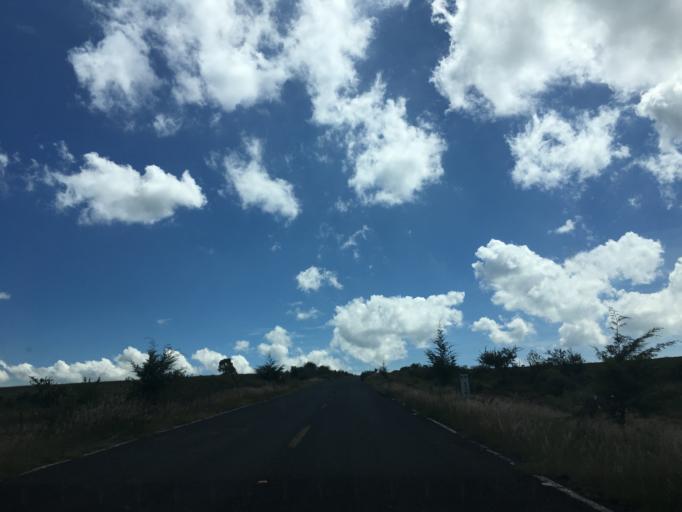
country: MX
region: Michoacan
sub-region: Morelia
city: Cuto de la Esperanza
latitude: 19.7724
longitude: -101.3803
